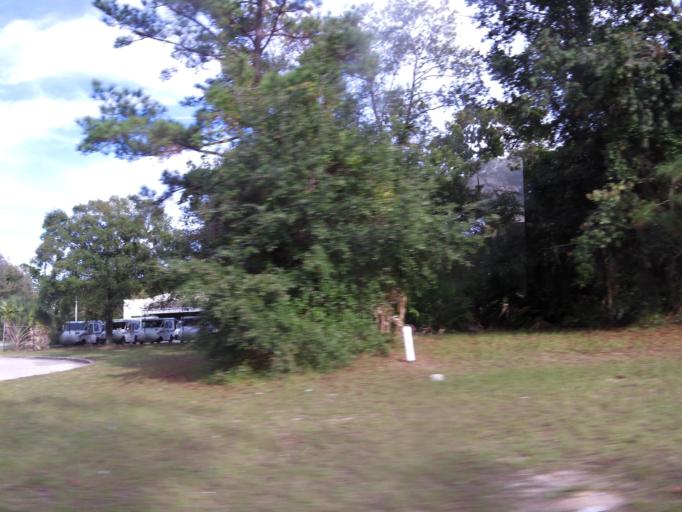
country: US
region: Florida
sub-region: Duval County
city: Jacksonville
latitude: 30.4290
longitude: -81.6483
